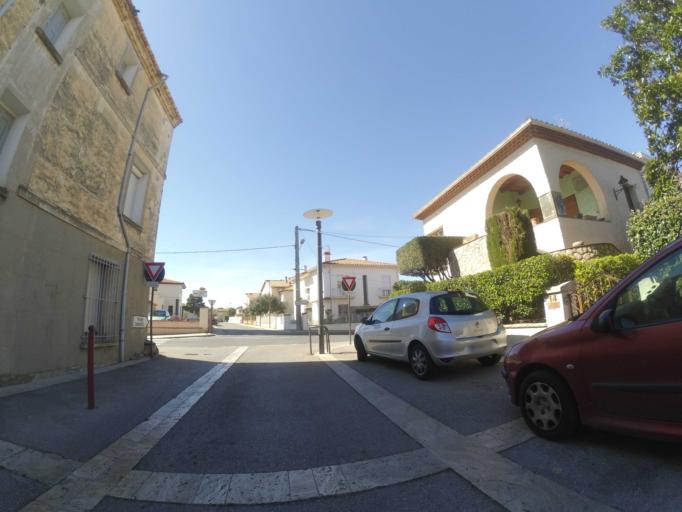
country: FR
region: Languedoc-Roussillon
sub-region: Departement des Pyrenees-Orientales
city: Toulouges
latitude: 42.6714
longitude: 2.8287
